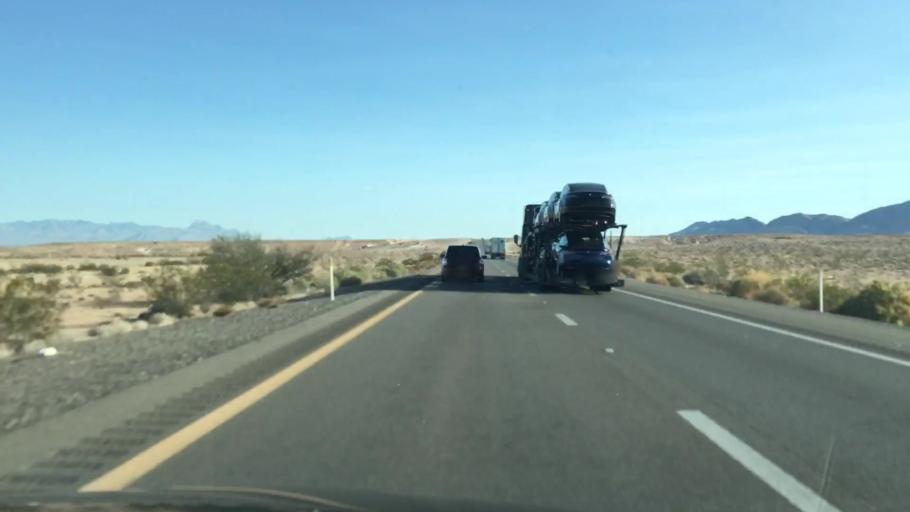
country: US
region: Nevada
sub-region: Clark County
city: Moapa Town
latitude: 36.5633
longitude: -114.6804
